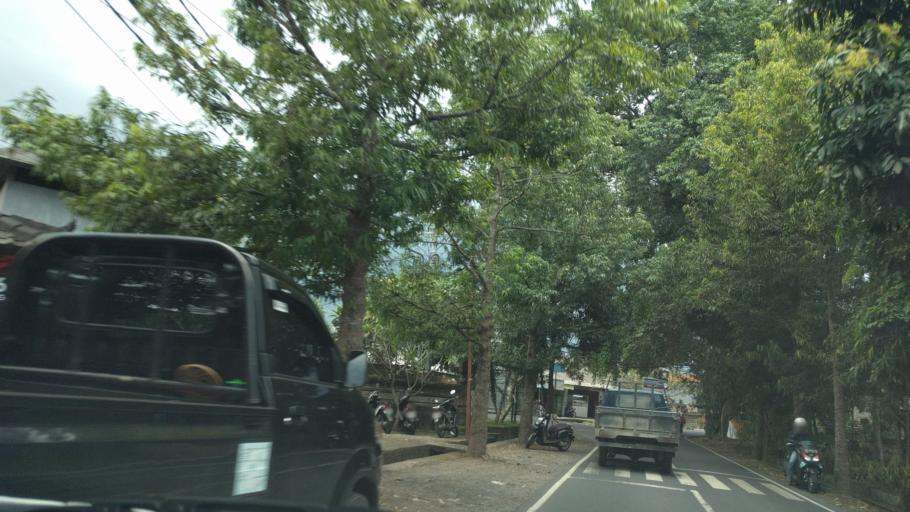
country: ID
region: Bali
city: Banjar Pande
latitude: -8.5193
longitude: 115.2400
